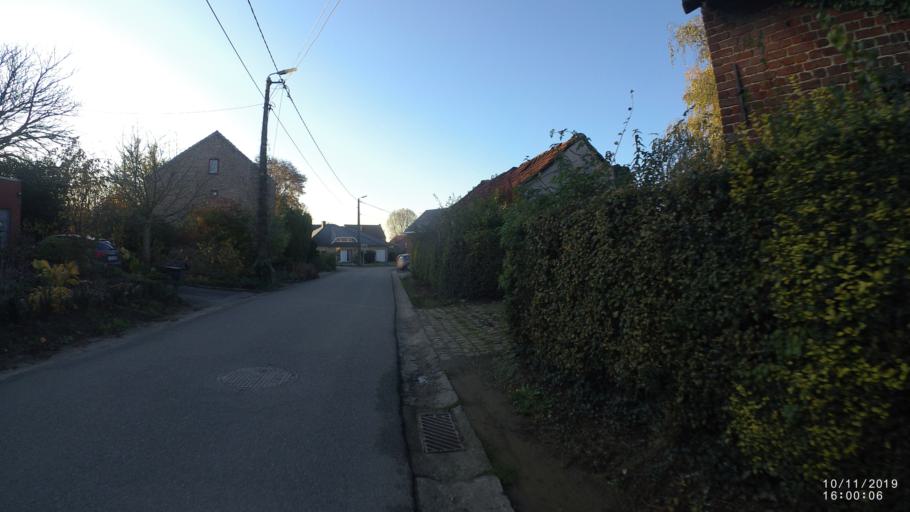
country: BE
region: Flanders
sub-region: Provincie Vlaams-Brabant
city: Lubbeek
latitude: 50.9027
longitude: 4.8793
